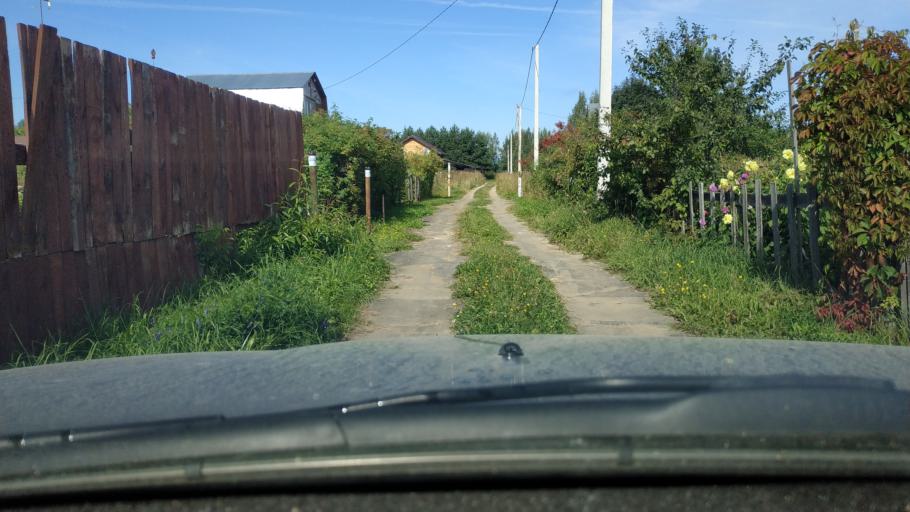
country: RU
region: Kostroma
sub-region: Kostromskoy Rayon
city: Kostroma
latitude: 57.7806
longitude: 40.7560
